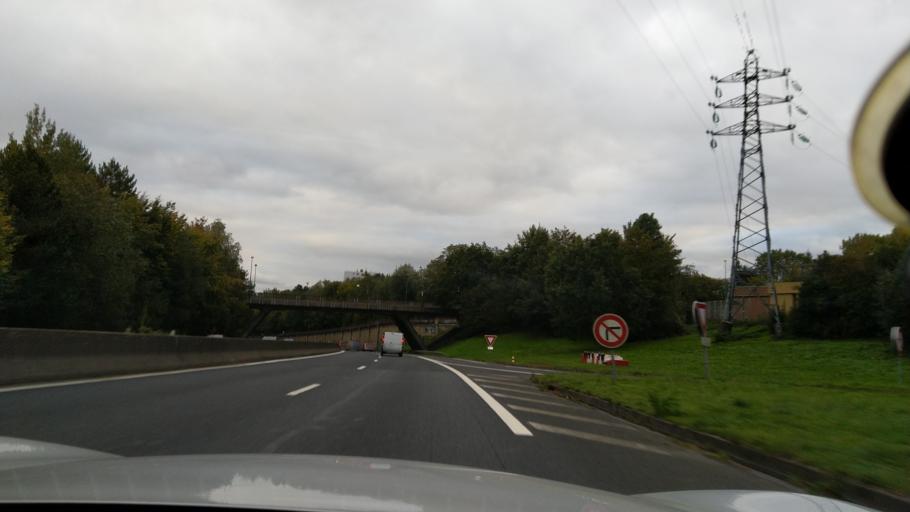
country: FR
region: Haute-Normandie
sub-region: Departement de la Seine-Maritime
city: Bois-Guillaume
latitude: 49.4681
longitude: 1.1333
